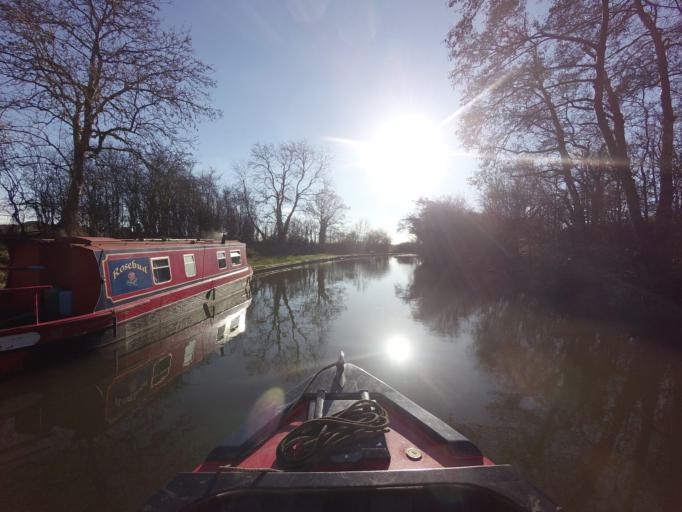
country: GB
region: England
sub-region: Northamptonshire
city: Long Buckby
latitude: 52.2446
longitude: -1.0840
